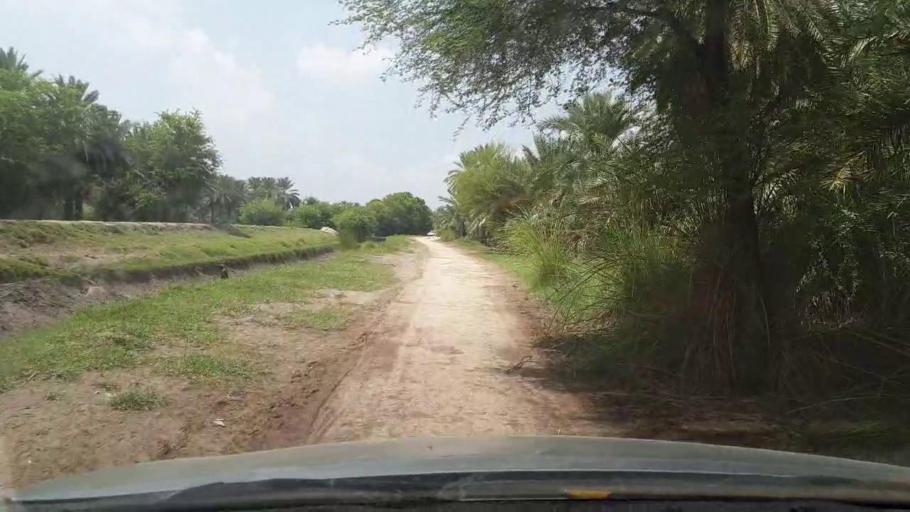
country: PK
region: Sindh
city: Khairpur
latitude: 27.4825
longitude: 68.7342
